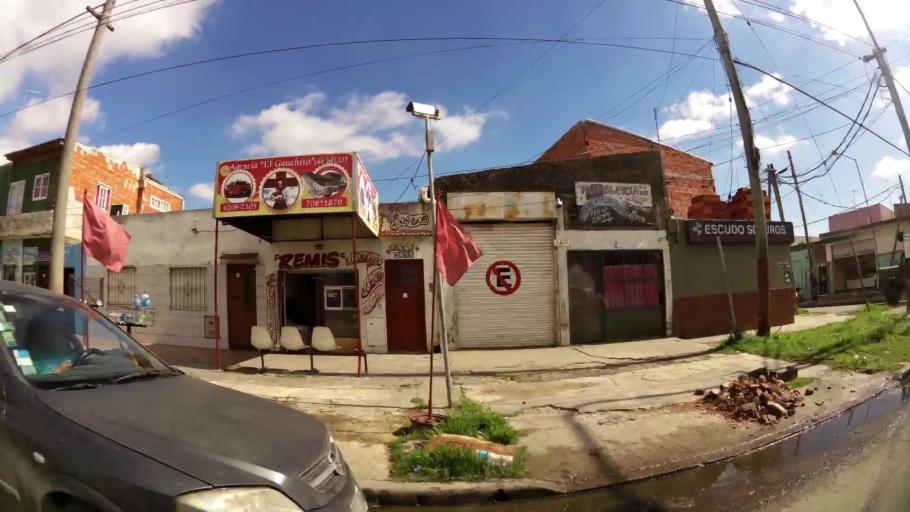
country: AR
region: Buenos Aires
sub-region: Partido de Lanus
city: Lanus
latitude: -34.6794
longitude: -58.4302
